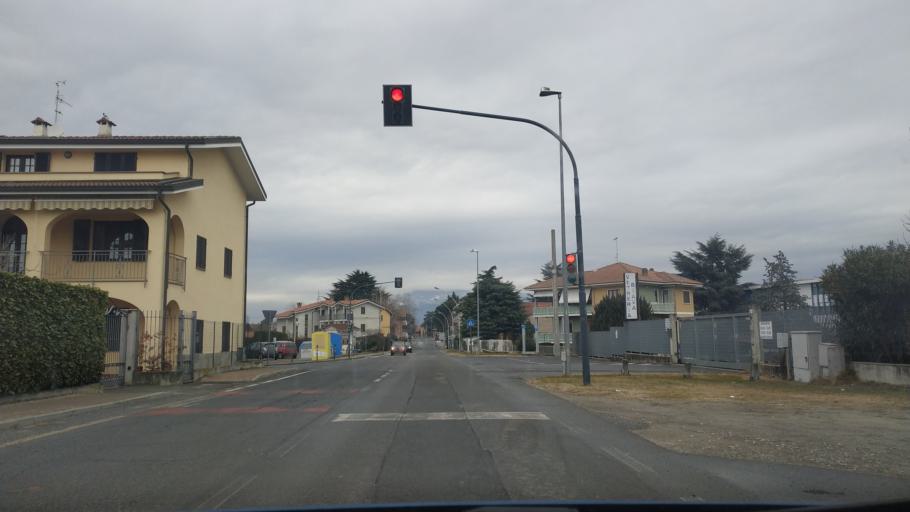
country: IT
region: Piedmont
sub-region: Provincia di Torino
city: Romano Canavese
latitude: 45.4249
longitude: 7.8826
